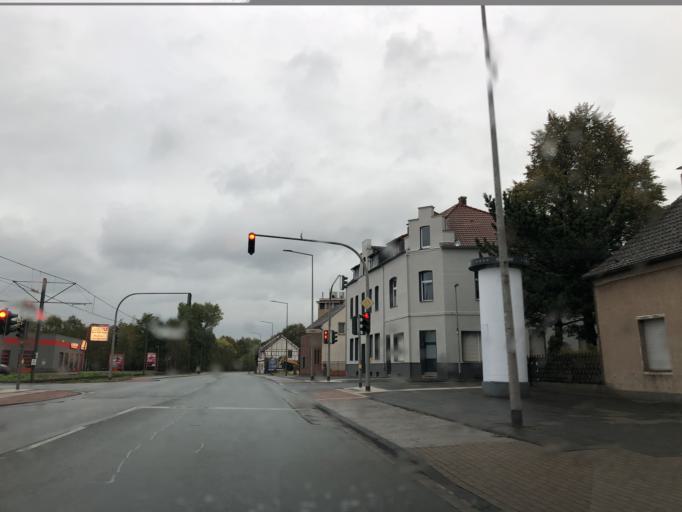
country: DE
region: North Rhine-Westphalia
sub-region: Regierungsbezirk Dusseldorf
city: Hochfeld
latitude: 51.3796
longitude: 6.7370
